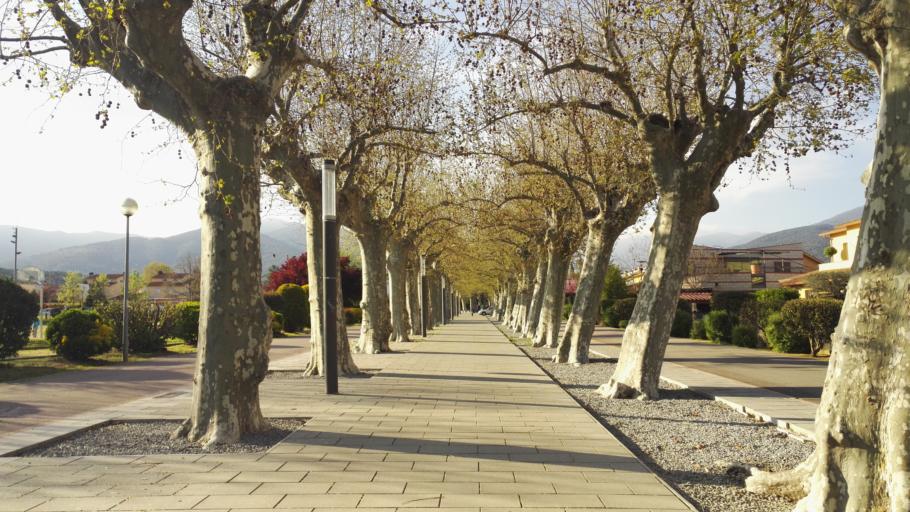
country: ES
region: Catalonia
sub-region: Provincia de Barcelona
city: Santa Maria de Palautordera
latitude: 41.6964
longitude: 2.4410
